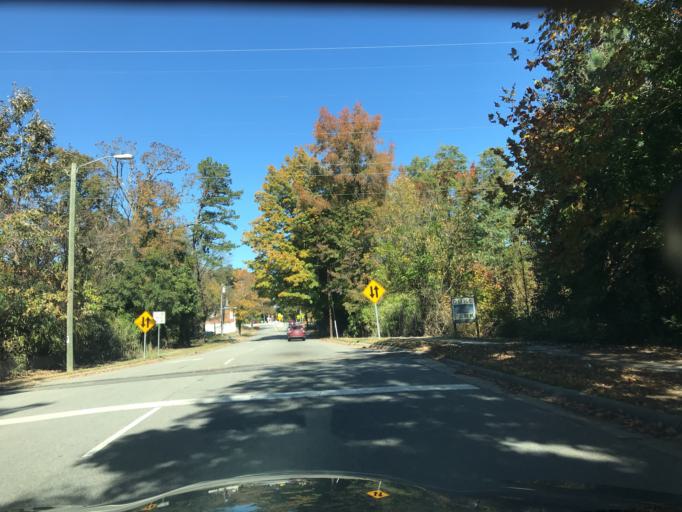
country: US
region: North Carolina
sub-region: Durham County
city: Durham
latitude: 36.0082
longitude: -78.8921
